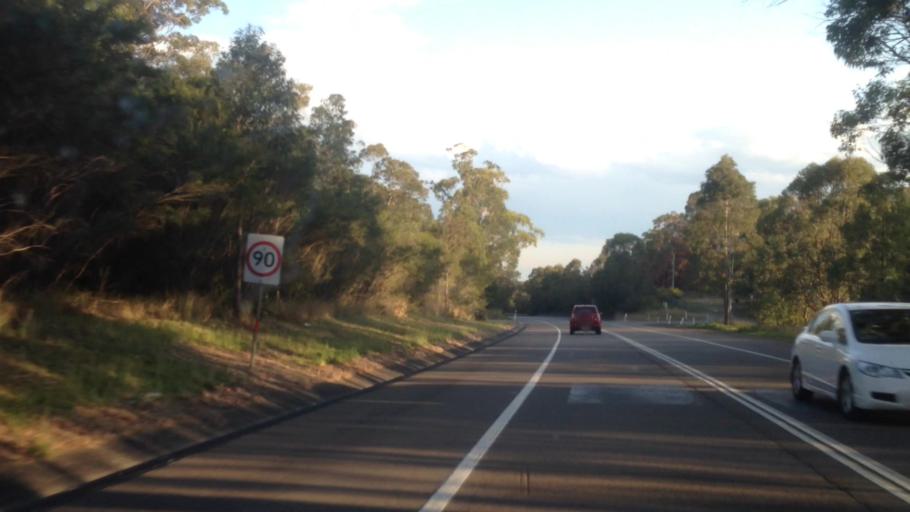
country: AU
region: New South Wales
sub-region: Lake Macquarie Shire
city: Dora Creek
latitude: -33.0061
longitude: 151.4892
